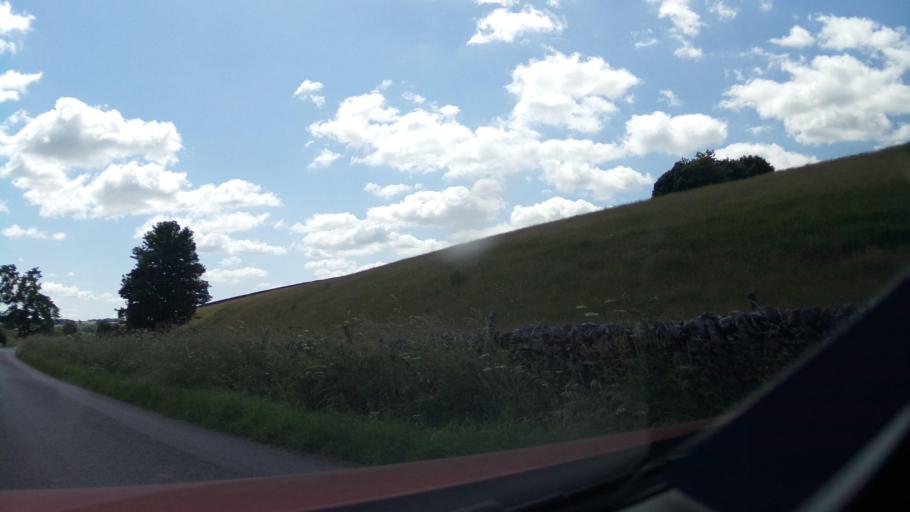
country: GB
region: England
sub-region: Derbyshire
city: Tideswell
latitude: 53.2070
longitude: -1.7798
